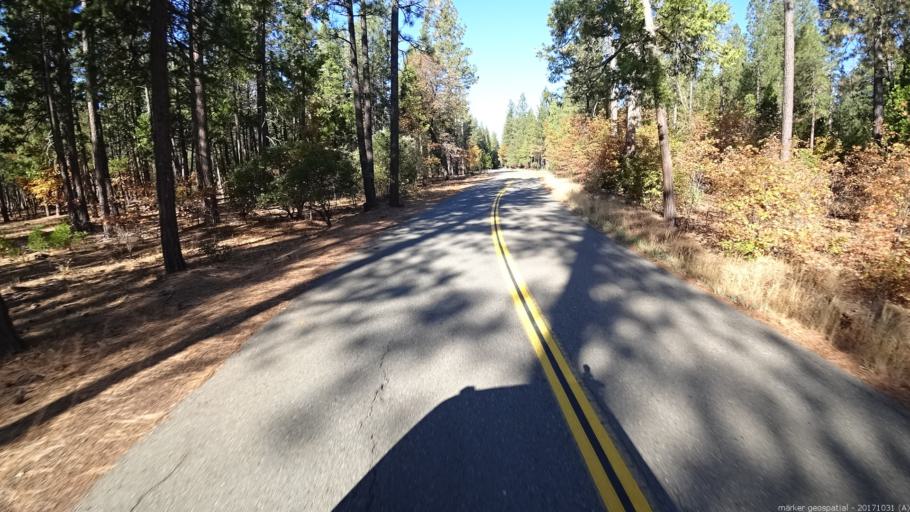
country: US
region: California
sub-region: Shasta County
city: Shingletown
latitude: 40.4849
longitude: -121.8802
